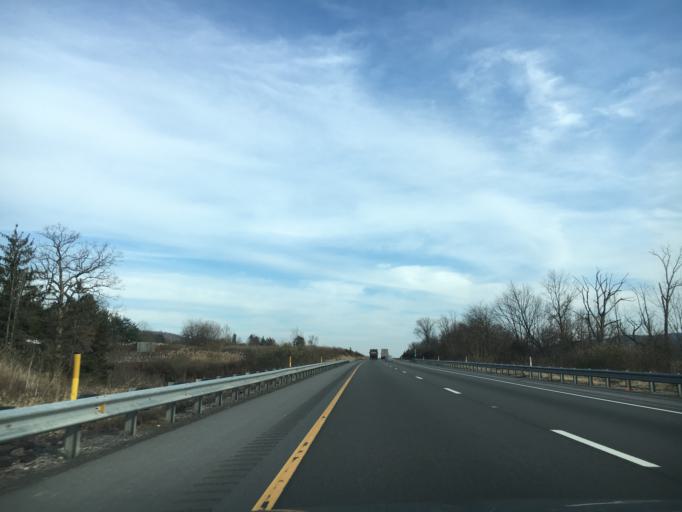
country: US
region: Pennsylvania
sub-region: Montour County
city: Danville
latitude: 40.9996
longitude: -76.6255
